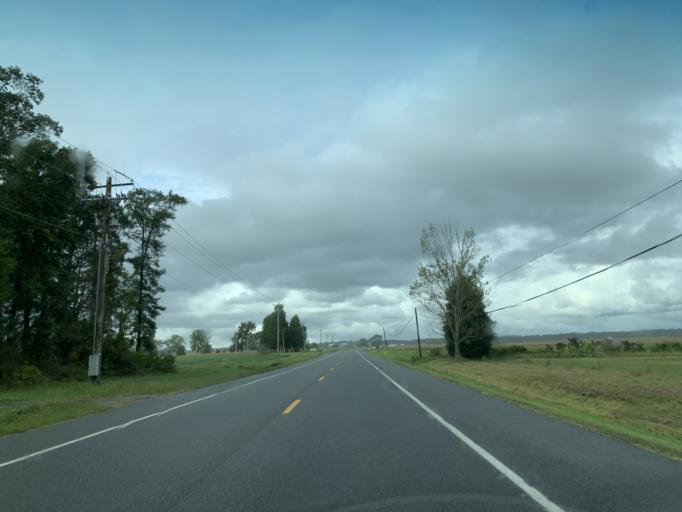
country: US
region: Maryland
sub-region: Caroline County
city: Ridgely
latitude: 38.9926
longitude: -75.8762
